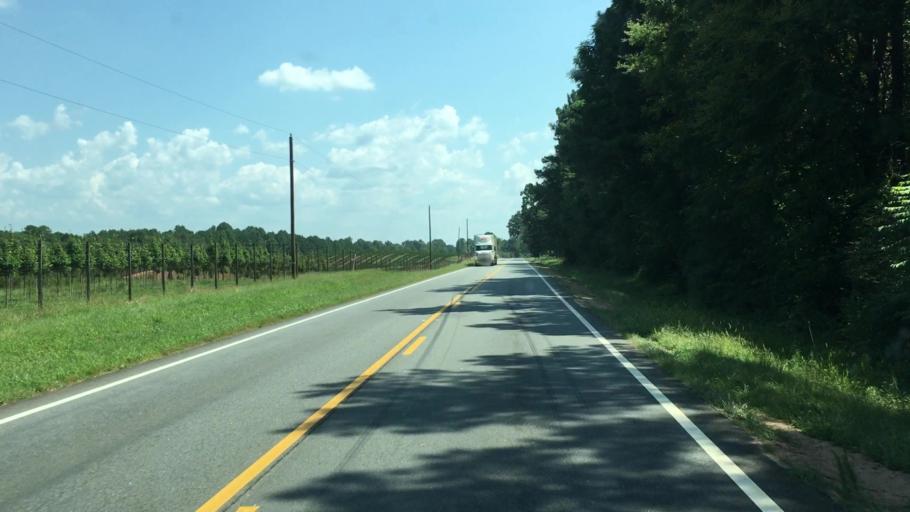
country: US
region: Georgia
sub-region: Oconee County
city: Watkinsville
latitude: 33.7486
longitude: -83.4338
